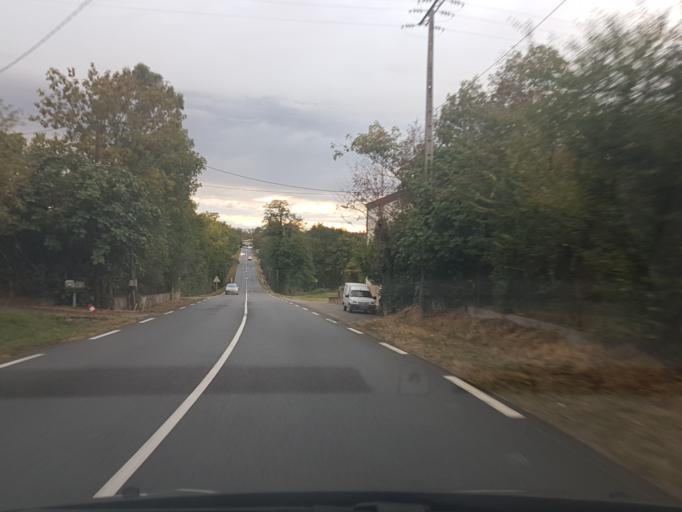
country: FR
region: Midi-Pyrenees
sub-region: Departement de l'Ariege
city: La Tour-du-Crieu
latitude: 43.0911
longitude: 1.7311
